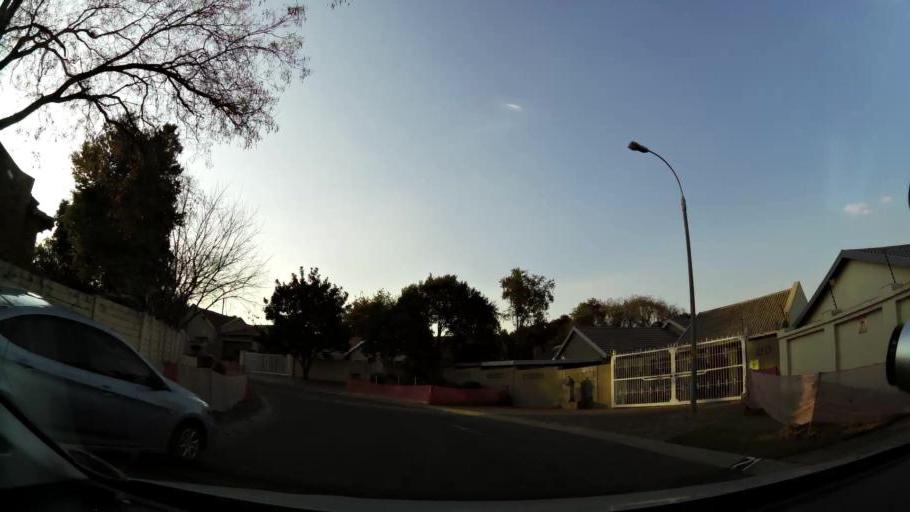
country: ZA
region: Gauteng
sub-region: City of Johannesburg Metropolitan Municipality
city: Modderfontein
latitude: -26.0812
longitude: 28.2190
